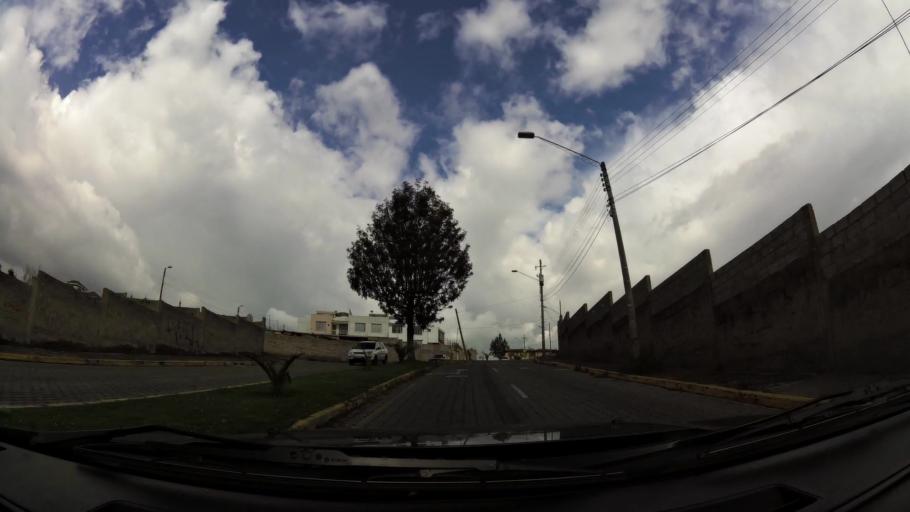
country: EC
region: Pichincha
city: Sangolqui
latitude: -0.3279
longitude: -78.4595
